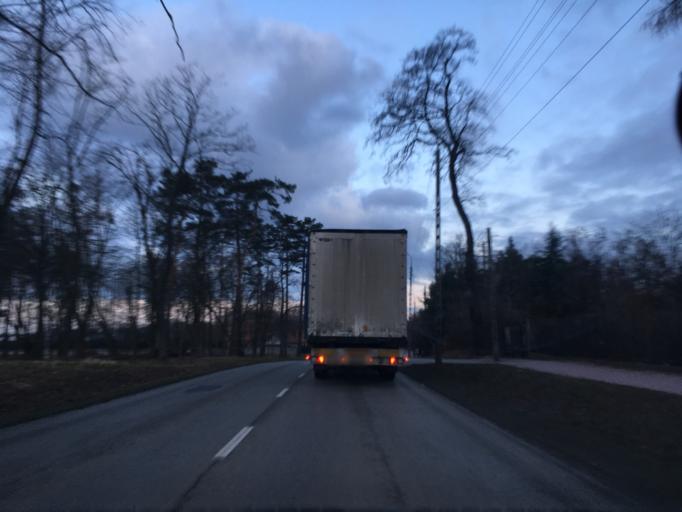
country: PL
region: Masovian Voivodeship
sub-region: Powiat grodziski
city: Grodzisk Mazowiecki
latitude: 52.0951
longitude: 20.6584
